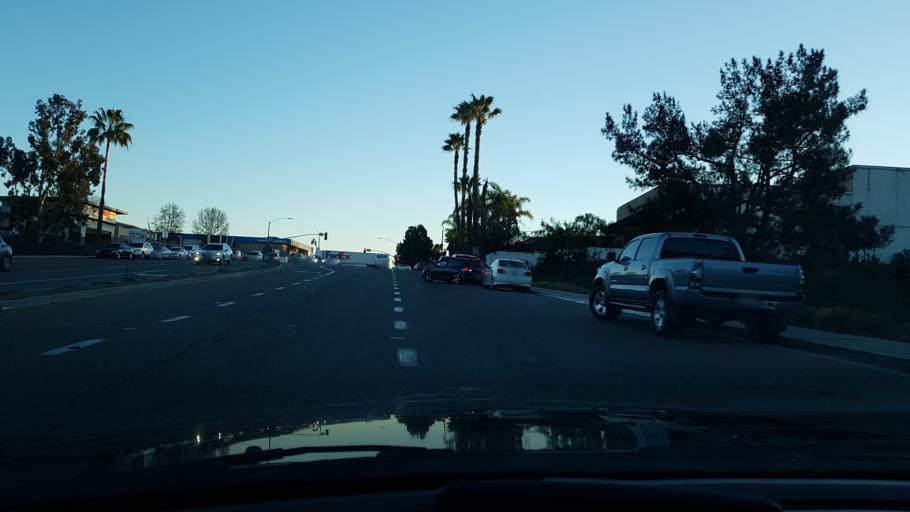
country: US
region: California
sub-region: San Diego County
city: La Jolla
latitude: 32.8794
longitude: -117.1726
